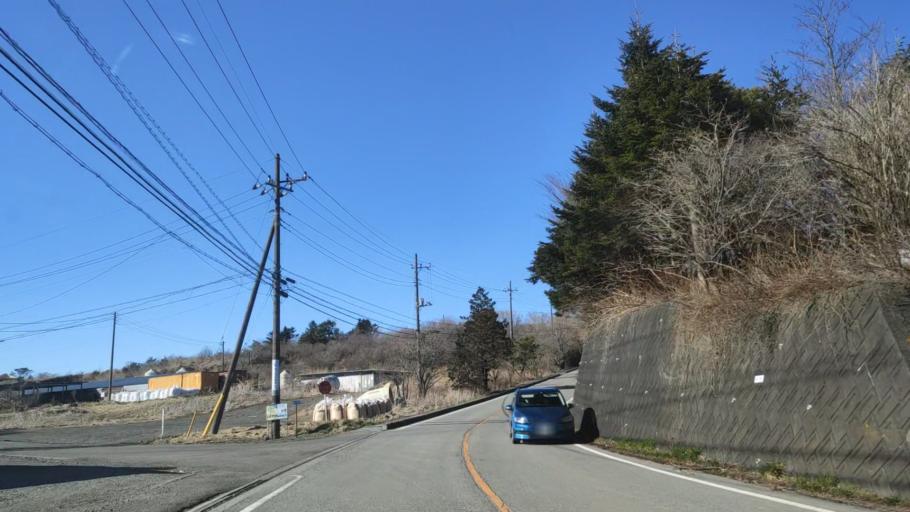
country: JP
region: Yamanashi
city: Fujikawaguchiko
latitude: 35.4200
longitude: 138.6244
